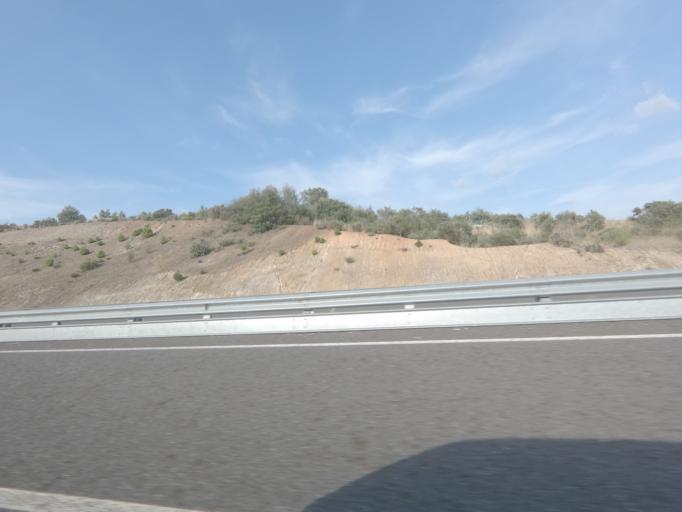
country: ES
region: Galicia
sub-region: Provincia de Ourense
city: Oimbra
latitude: 41.8482
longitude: -7.4125
